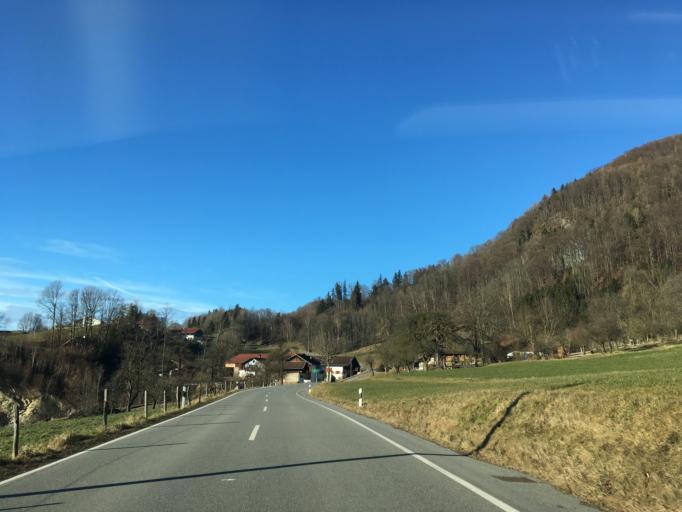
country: DE
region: Bavaria
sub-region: Upper Bavaria
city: Nussdorf am Inn
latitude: 47.7193
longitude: 12.1648
